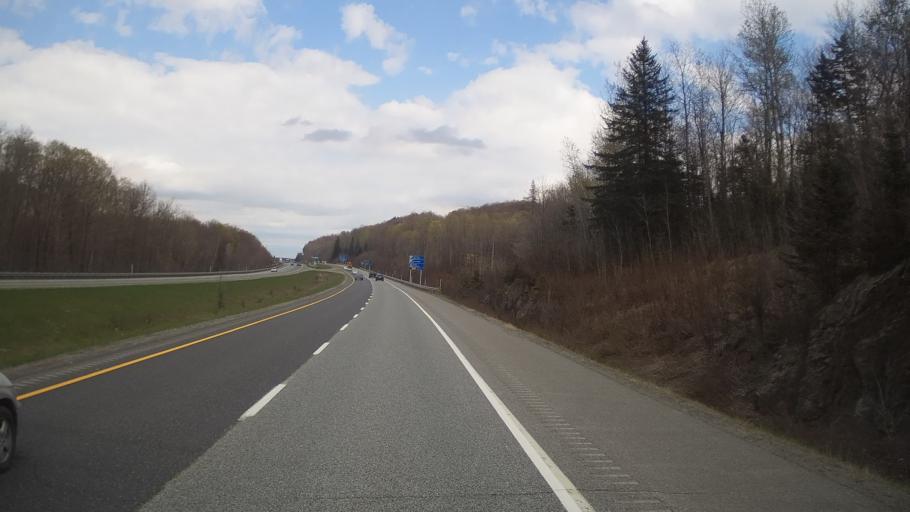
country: CA
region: Quebec
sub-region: Estrie
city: Magog
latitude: 45.2892
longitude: -72.2543
